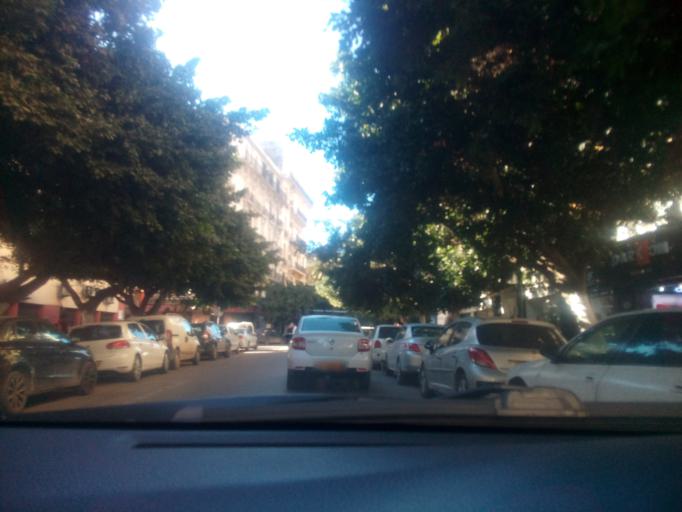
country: DZ
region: Oran
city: Oran
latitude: 35.7049
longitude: -0.6369
